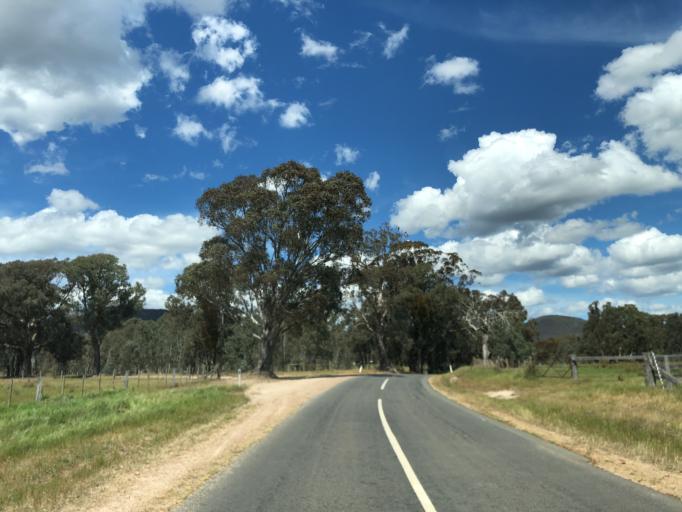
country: AU
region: Victoria
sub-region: Benalla
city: Benalla
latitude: -36.7380
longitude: 146.1150
